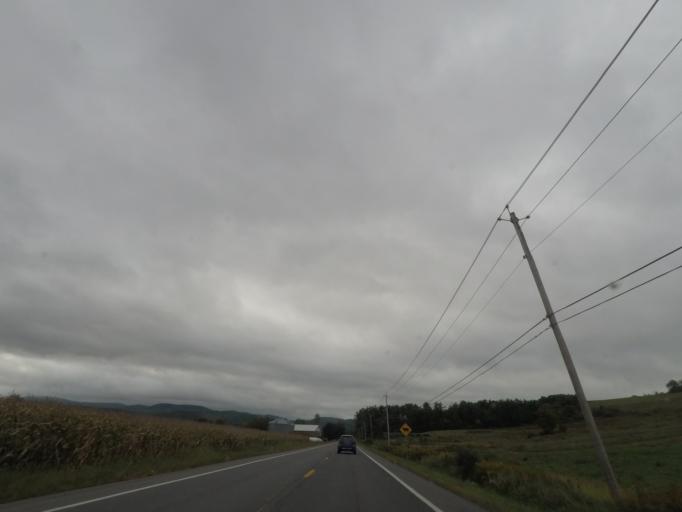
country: US
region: New York
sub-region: Rensselaer County
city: Hoosick Falls
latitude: 42.8703
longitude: -73.3515
